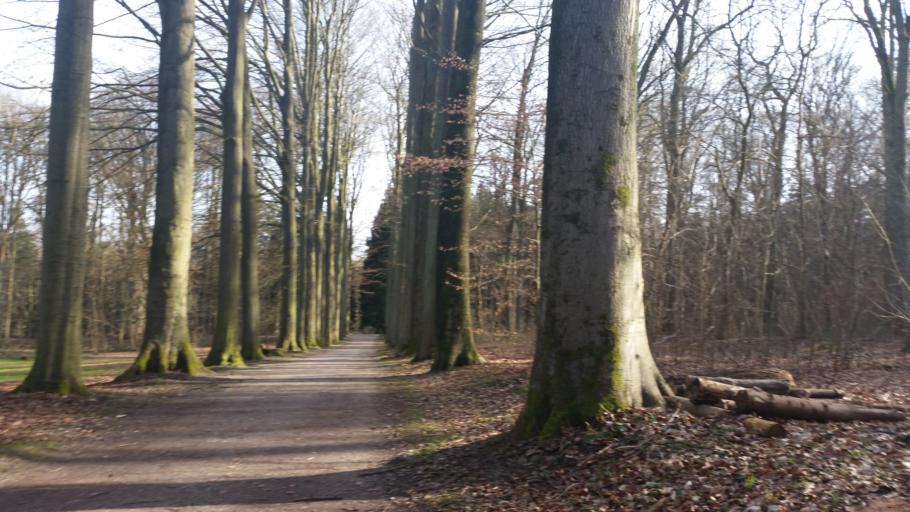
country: BE
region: Flanders
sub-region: Provincie Vlaams-Brabant
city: Tervuren
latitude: 50.8106
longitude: 4.5162
